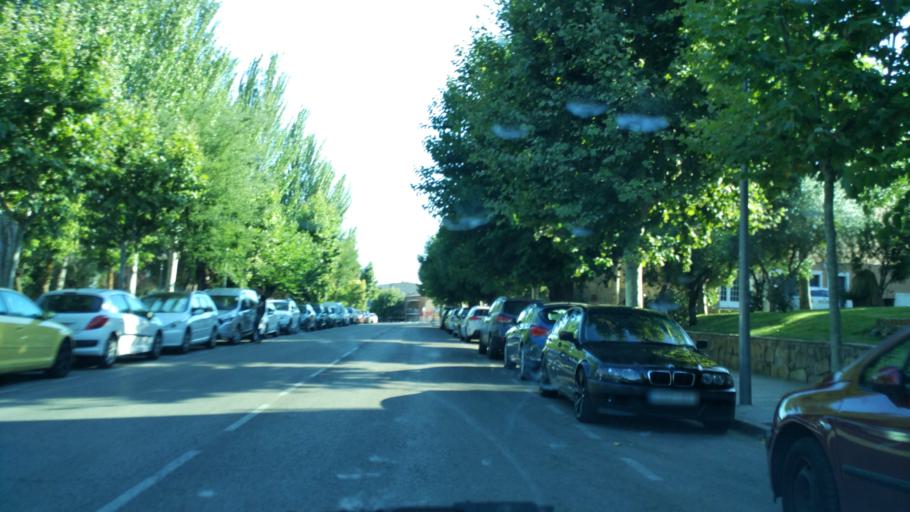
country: ES
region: Madrid
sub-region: Provincia de Madrid
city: San Agustin de Guadalix
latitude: 40.6817
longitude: -3.6133
